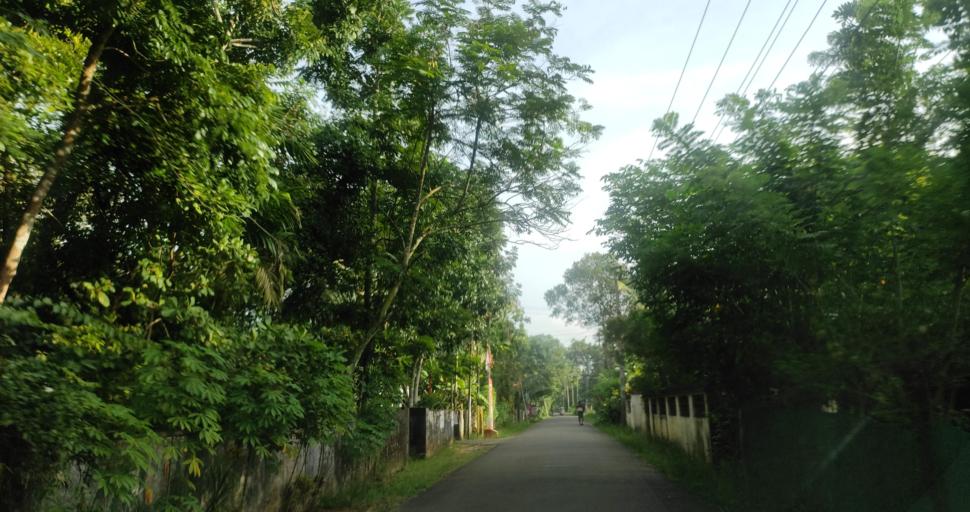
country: IN
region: Kerala
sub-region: Alappuzha
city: Shertallai
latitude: 9.6190
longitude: 76.3417
